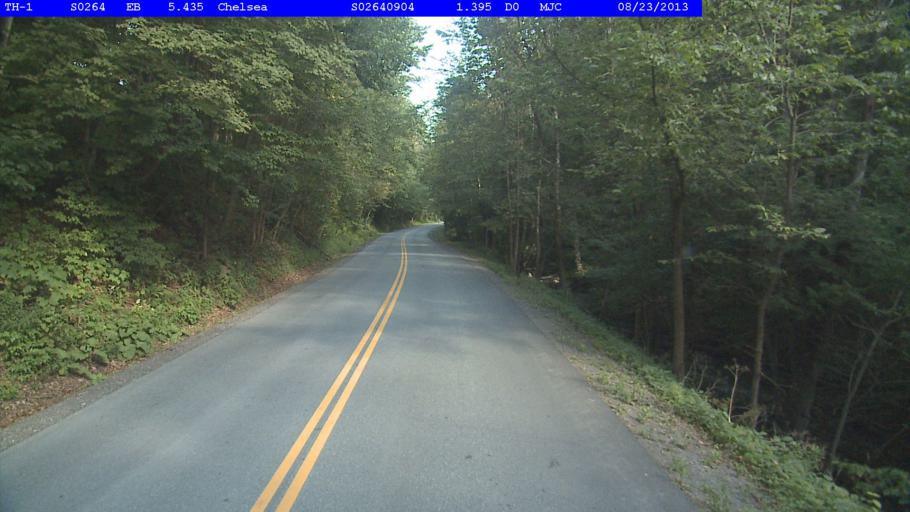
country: US
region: Vermont
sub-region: Orange County
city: Chelsea
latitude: 43.9727
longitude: -72.4861
